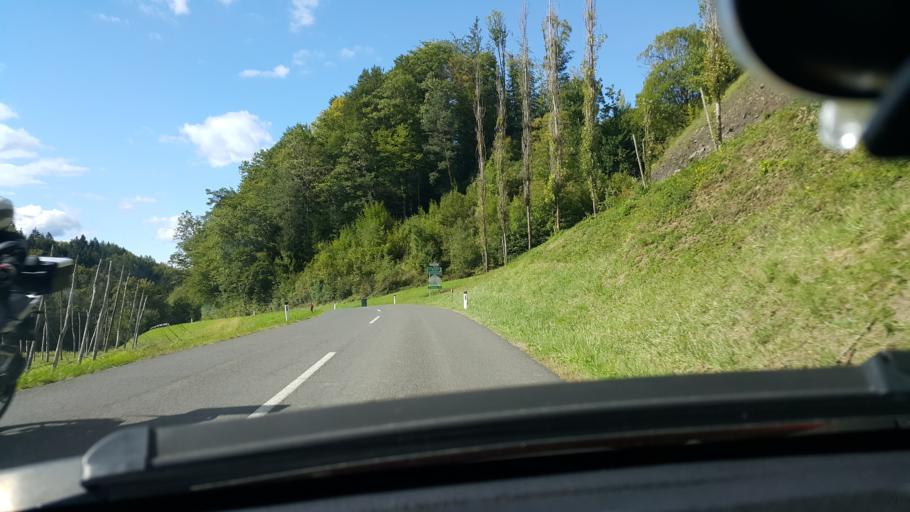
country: AT
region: Styria
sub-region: Politischer Bezirk Leibnitz
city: Leutschach
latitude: 46.6470
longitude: 15.4935
